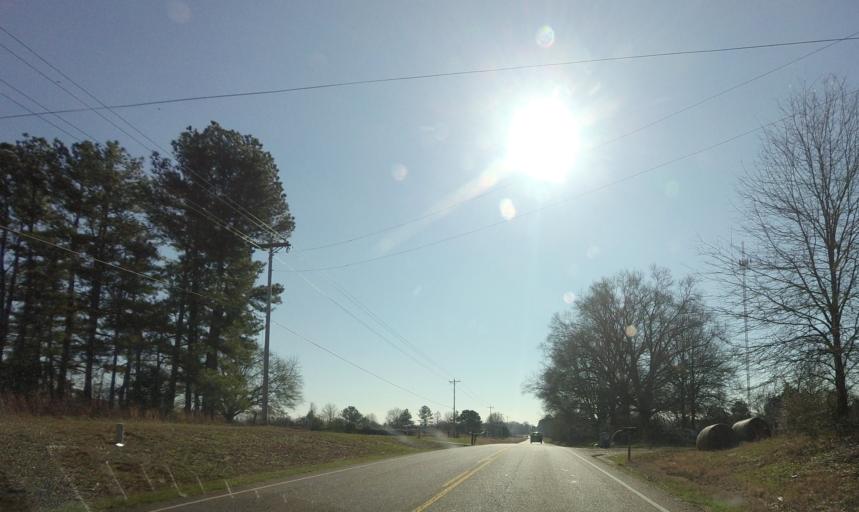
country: US
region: Tennessee
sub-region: Shelby County
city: Collierville
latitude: 34.9701
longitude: -89.6889
